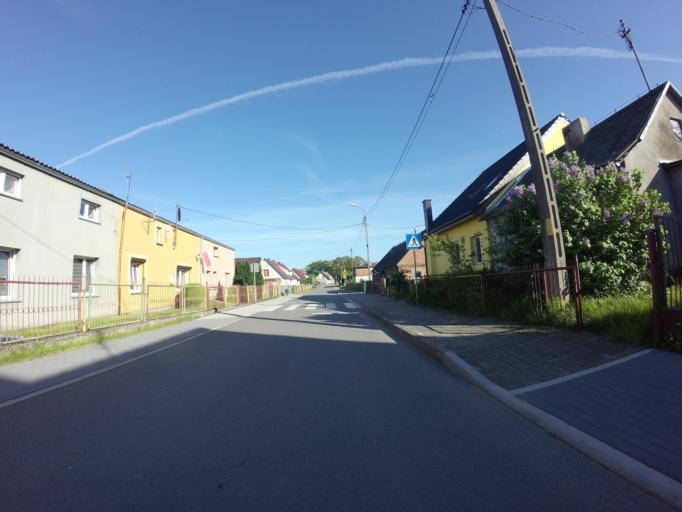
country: PL
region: West Pomeranian Voivodeship
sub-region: Powiat choszczenski
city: Pelczyce
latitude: 53.1199
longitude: 15.3202
